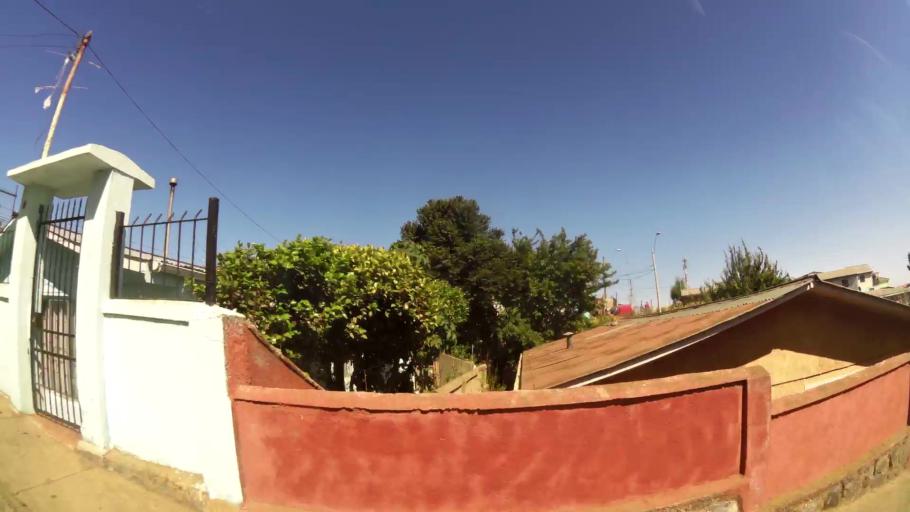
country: CL
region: Valparaiso
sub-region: Provincia de Valparaiso
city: Valparaiso
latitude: -33.0517
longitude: -71.6456
